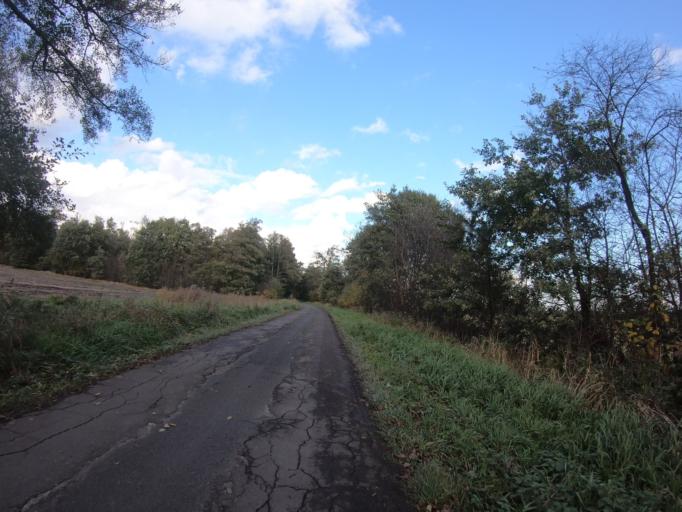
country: DE
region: Lower Saxony
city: Wagenhoff
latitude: 52.5415
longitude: 10.5554
